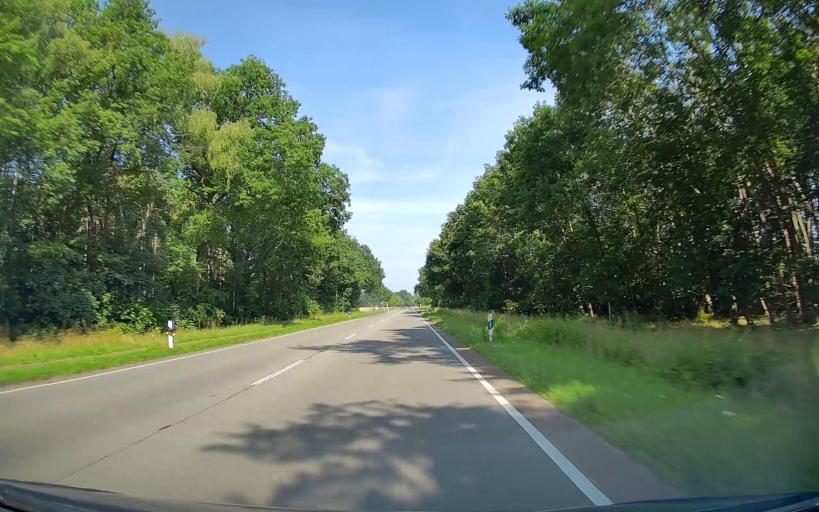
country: DE
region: Lower Saxony
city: Bosel
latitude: 52.9754
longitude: 7.9079
